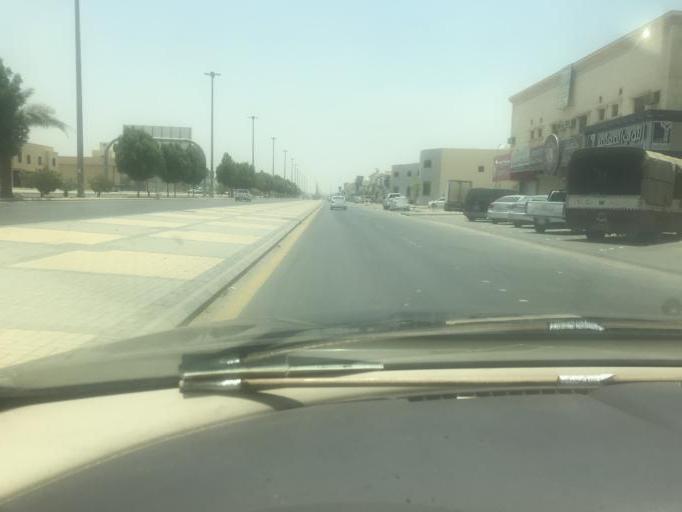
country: SA
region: Ar Riyad
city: Riyadh
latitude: 24.8203
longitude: 46.7514
